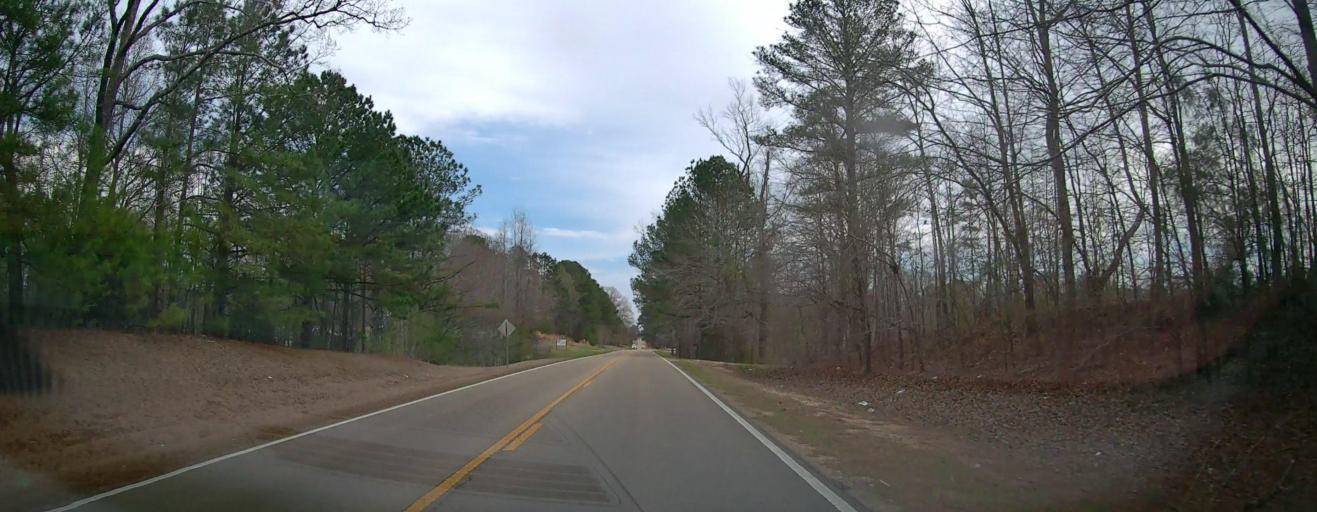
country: US
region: Mississippi
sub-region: Itawamba County
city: Mantachie
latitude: 34.2572
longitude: -88.5025
